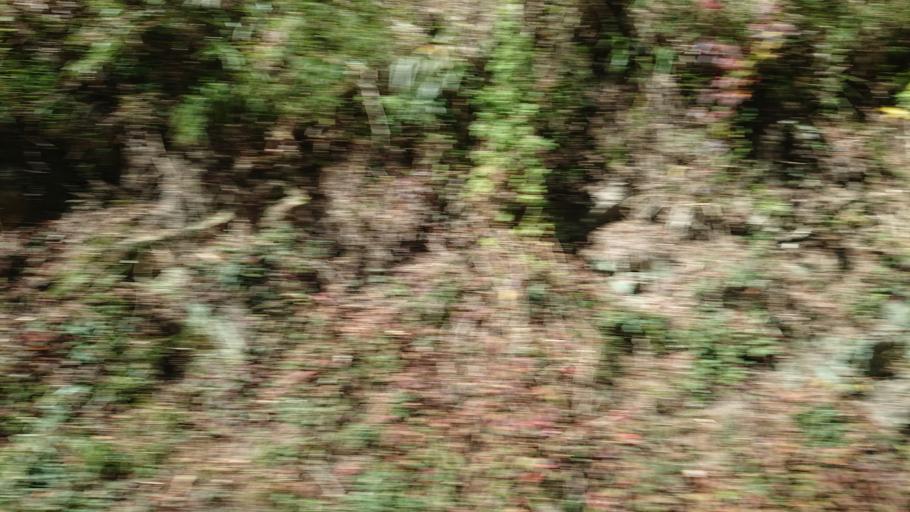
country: TW
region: Taiwan
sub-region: Hualien
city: Hualian
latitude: 24.3468
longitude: 121.3099
